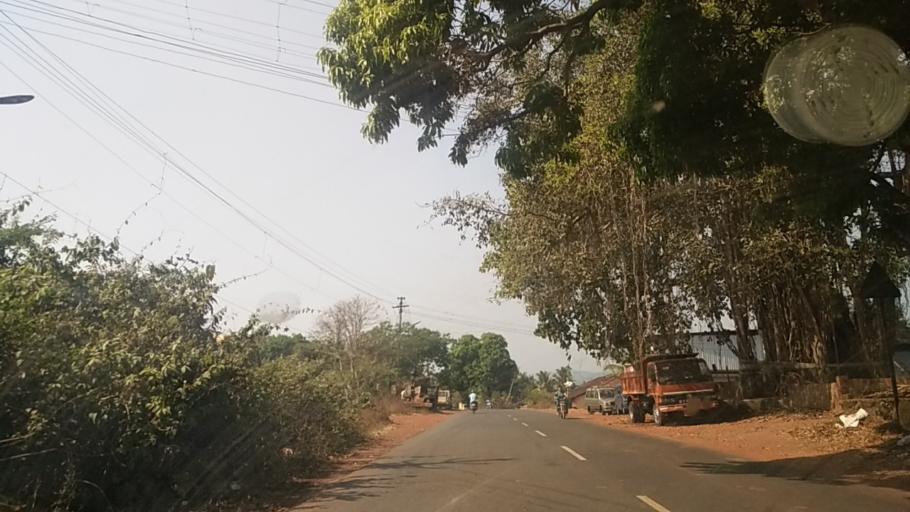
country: IN
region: Goa
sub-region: North Goa
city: Carapur
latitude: 15.5803
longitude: 73.9708
